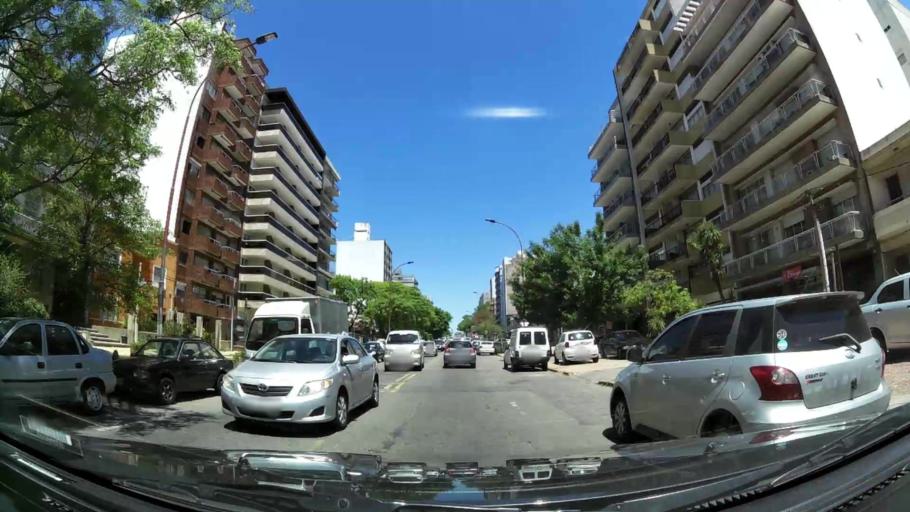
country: UY
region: Montevideo
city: Montevideo
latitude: -34.9008
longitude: -56.1599
